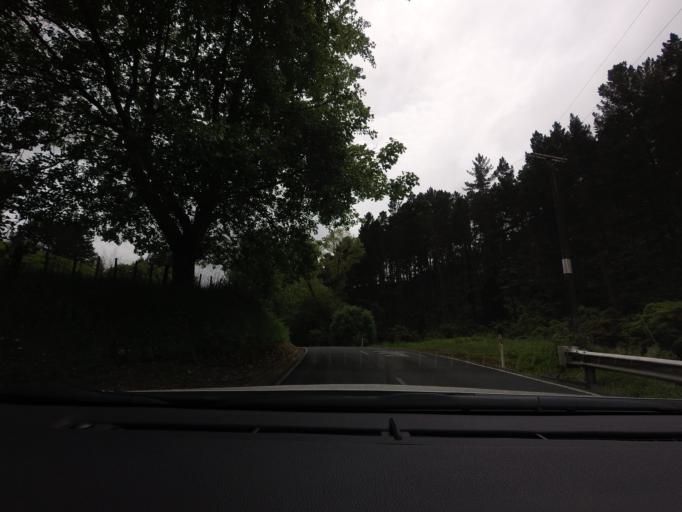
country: NZ
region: Auckland
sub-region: Auckland
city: Warkworth
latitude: -36.4993
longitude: 174.6279
